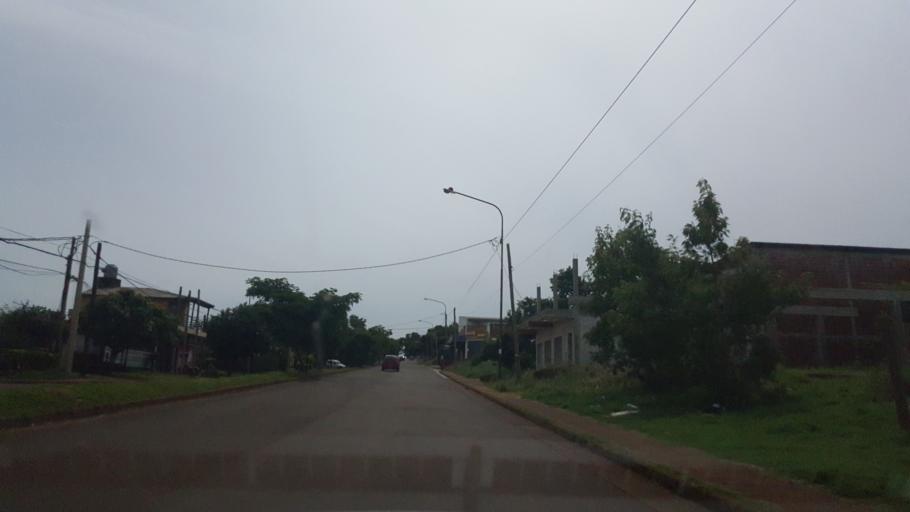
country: AR
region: Misiones
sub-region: Departamento de Capital
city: Posadas
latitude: -27.3855
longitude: -55.9418
